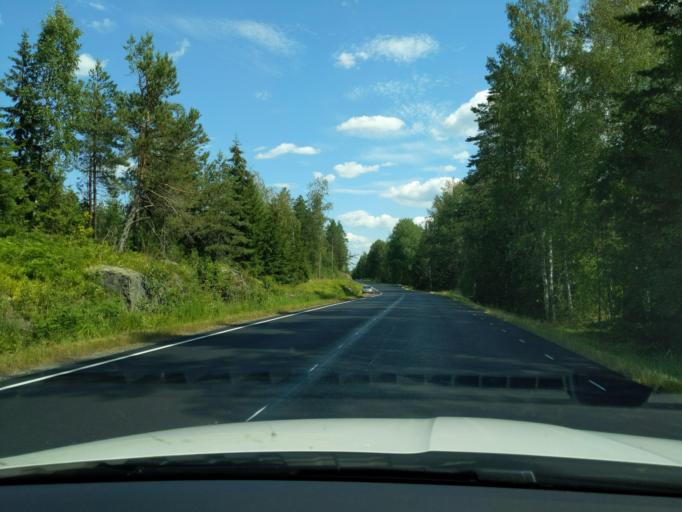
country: FI
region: Paijanne Tavastia
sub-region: Lahti
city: Nastola
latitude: 61.0853
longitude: 25.8453
